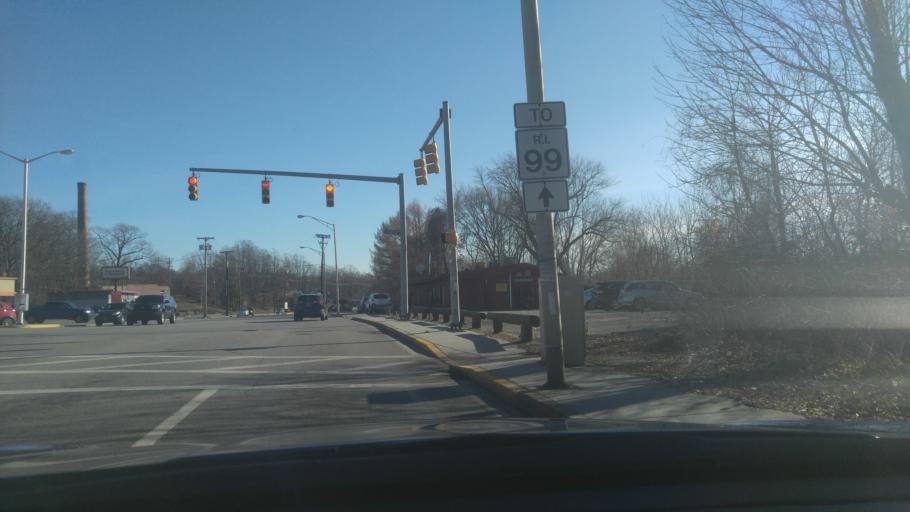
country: US
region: Rhode Island
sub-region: Providence County
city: Woonsocket
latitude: 42.0050
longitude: -71.4993
